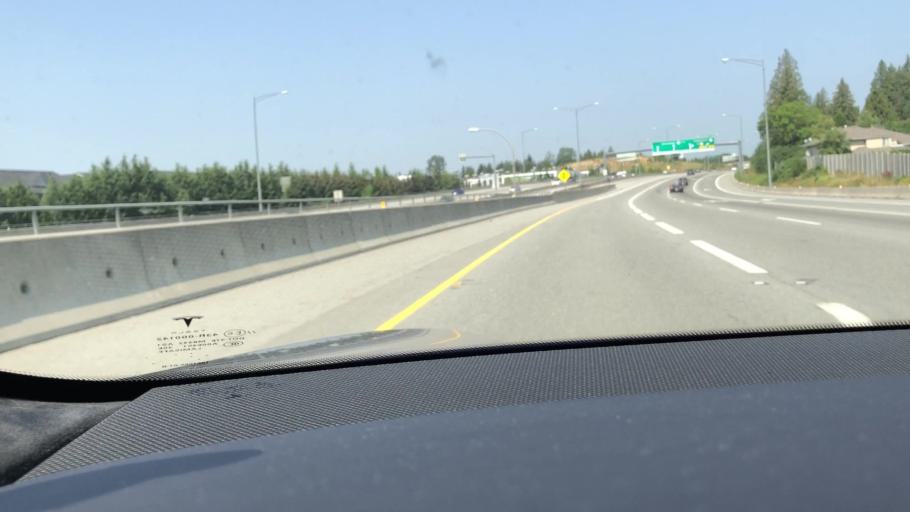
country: CA
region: British Columbia
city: Coquitlam
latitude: 49.1959
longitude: -122.7907
